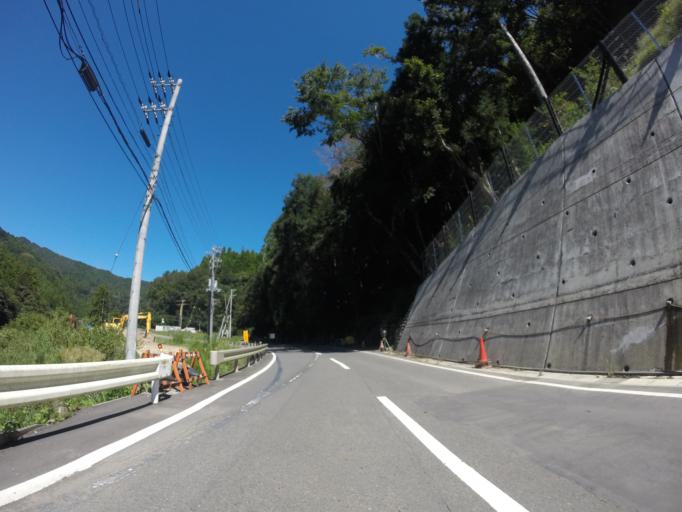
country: JP
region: Shizuoka
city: Kanaya
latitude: 34.9157
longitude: 138.1301
